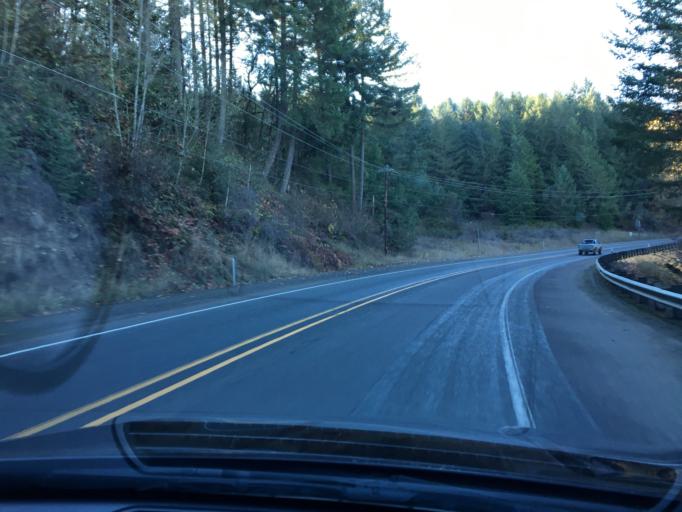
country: US
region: Oregon
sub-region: Douglas County
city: Glide
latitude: 43.2962
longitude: -123.1047
